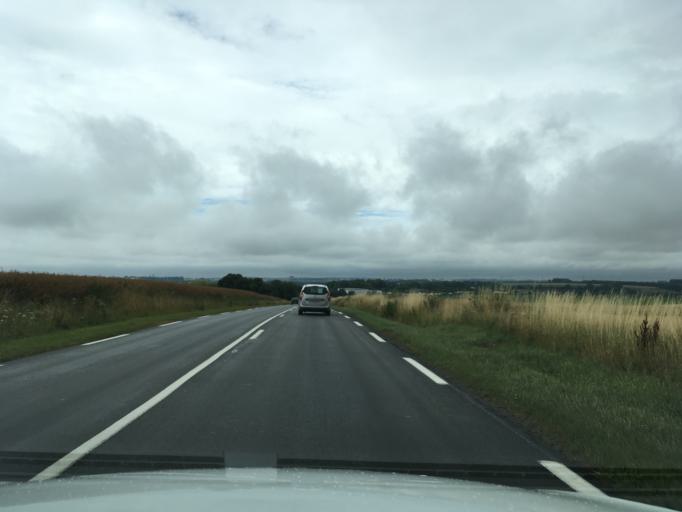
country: FR
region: Picardie
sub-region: Departement de l'Aisne
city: Homblieres
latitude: 49.8455
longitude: 3.3888
